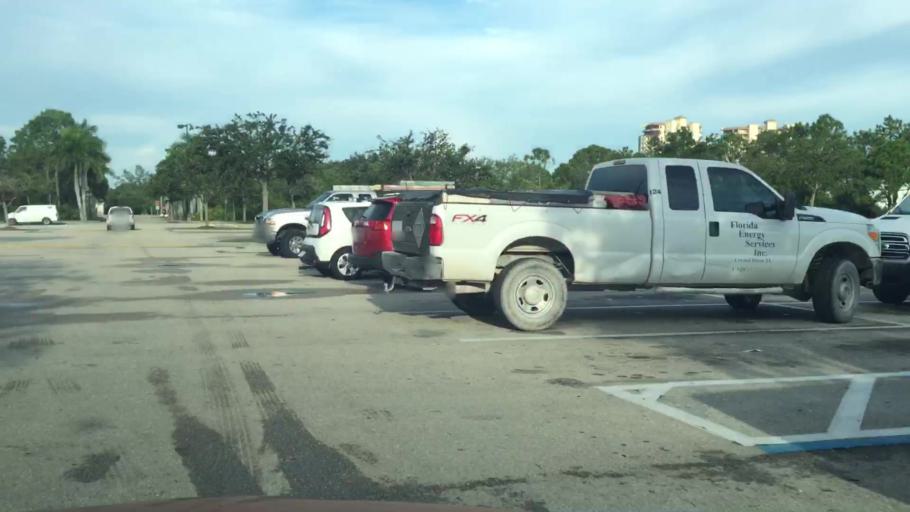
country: US
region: Florida
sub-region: Lee County
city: Villas
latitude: 26.5300
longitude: -81.8684
